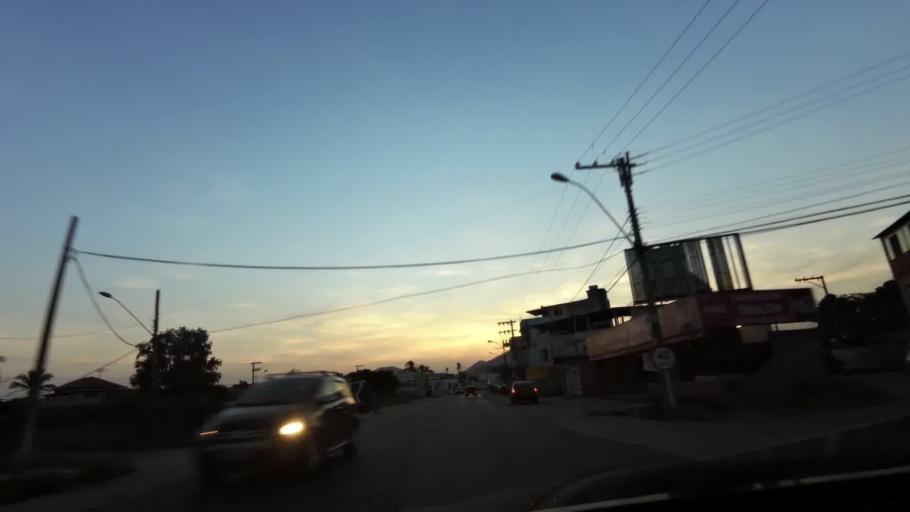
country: BR
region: Espirito Santo
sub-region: Guarapari
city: Guarapari
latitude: -20.6244
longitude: -40.4483
